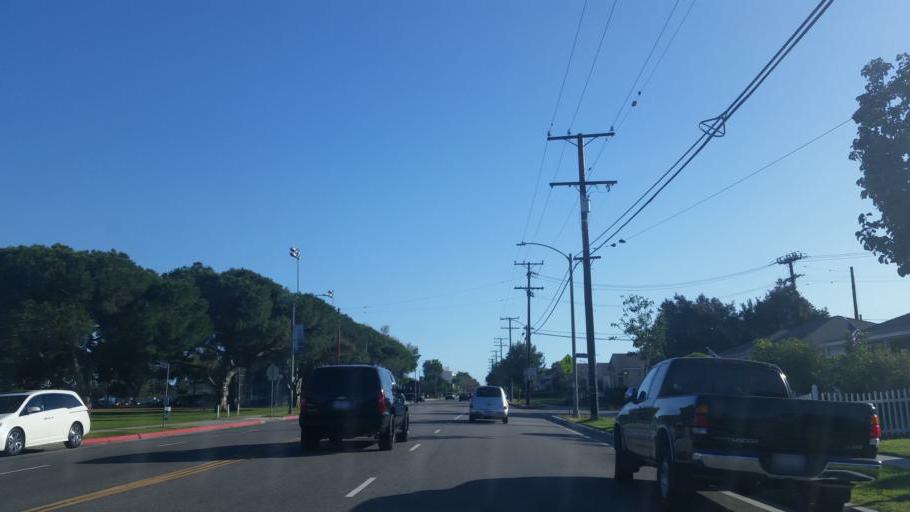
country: US
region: California
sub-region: Los Angeles County
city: Lakewood
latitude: 33.8580
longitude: -118.1338
